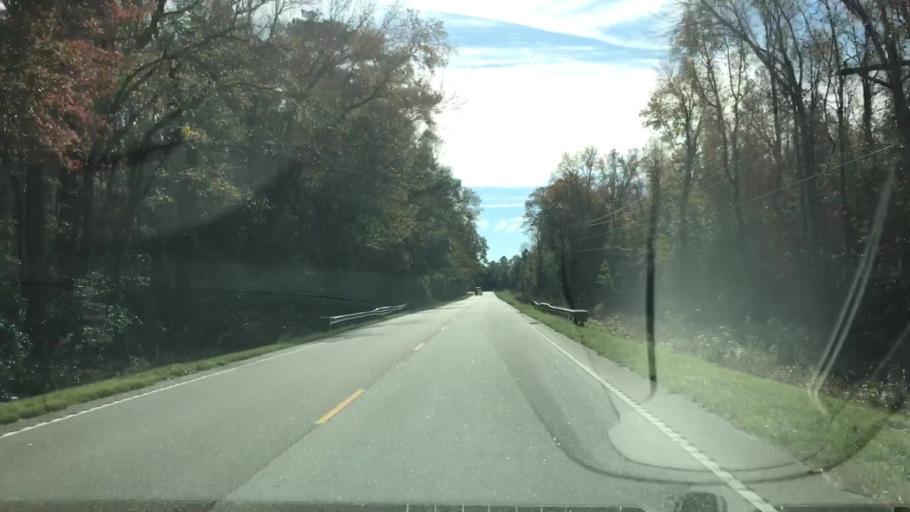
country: US
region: South Carolina
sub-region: Colleton County
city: Walterboro
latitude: 32.8398
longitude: -80.5877
